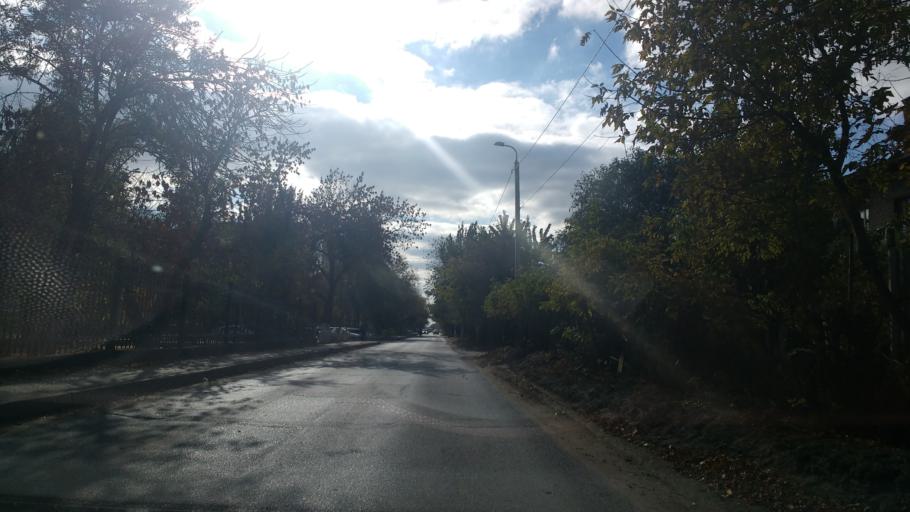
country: RU
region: Volgograd
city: Vodstroy
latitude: 48.7870
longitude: 44.5794
